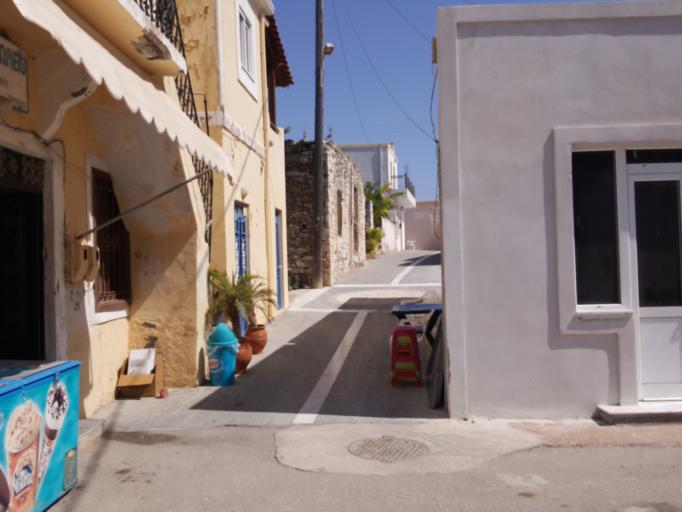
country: GR
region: South Aegean
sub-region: Nomos Dodekanisou
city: Lardos
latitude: 35.9539
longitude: 27.7684
